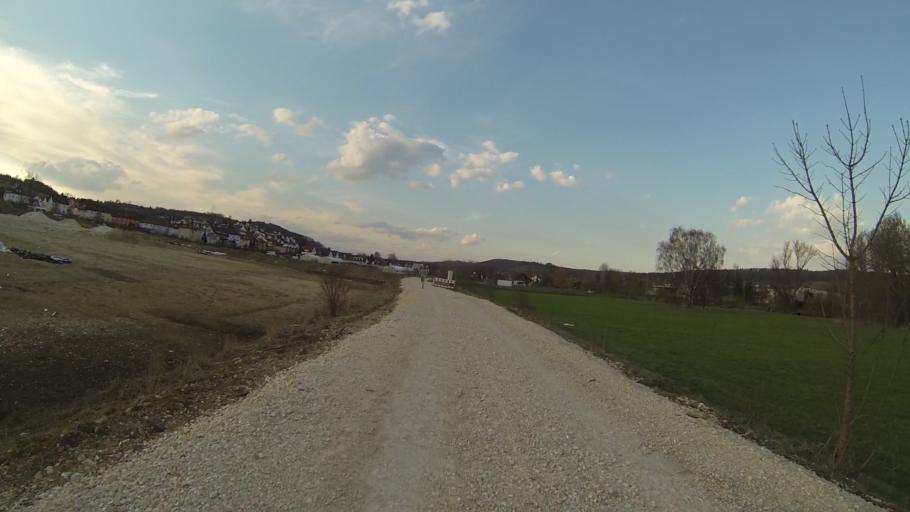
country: DE
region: Baden-Wuerttemberg
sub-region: Regierungsbezirk Stuttgart
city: Heidenheim an der Brenz
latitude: 48.6958
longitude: 10.1621
